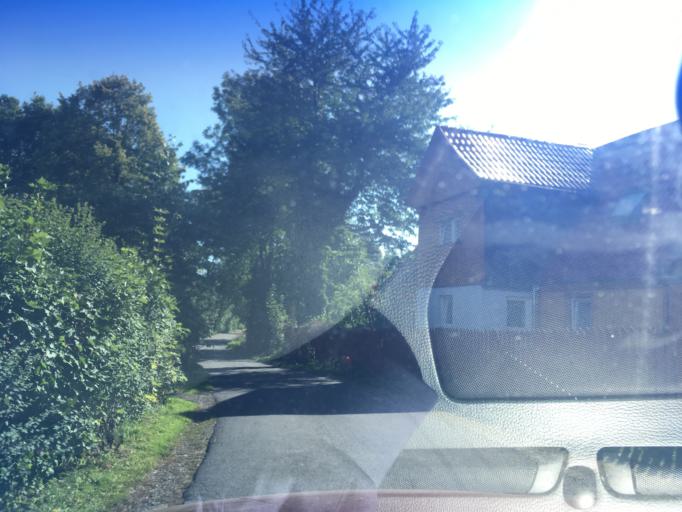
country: PL
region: Lower Silesian Voivodeship
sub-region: Powiat lubanski
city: Swieradow-Zdroj
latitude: 50.9572
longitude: 15.3183
